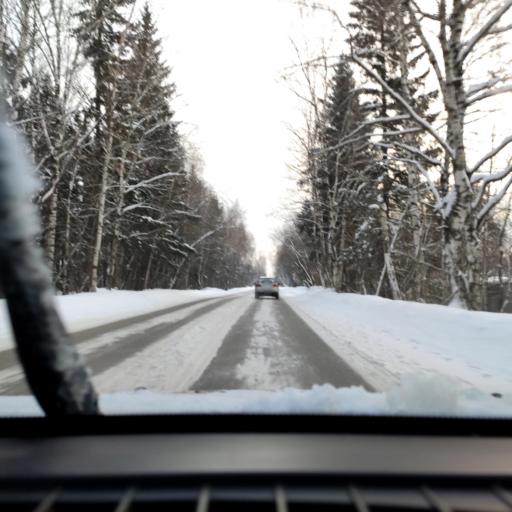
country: RU
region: Perm
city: Overyata
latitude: 58.0528
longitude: 55.8839
